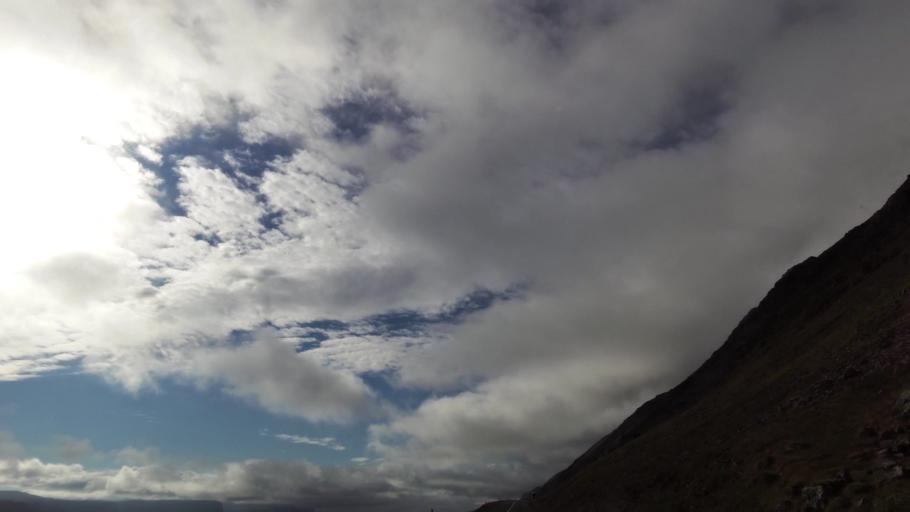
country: IS
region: West
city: Olafsvik
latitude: 65.5551
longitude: -23.8972
